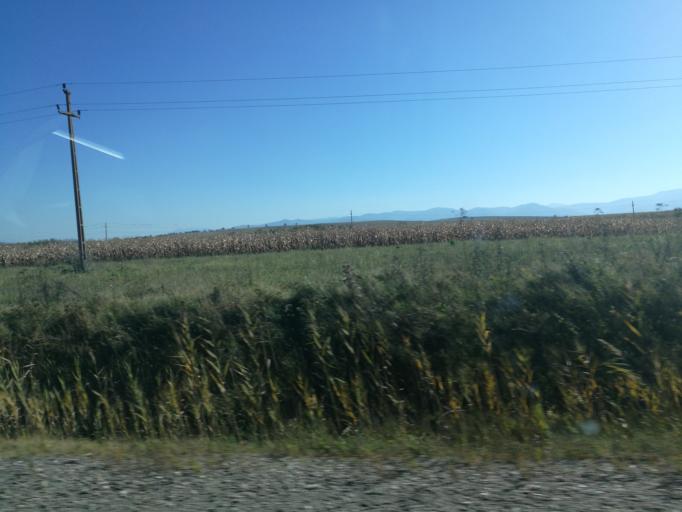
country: RO
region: Brasov
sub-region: Comuna Mandra
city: Mandra
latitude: 45.8234
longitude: 25.0843
